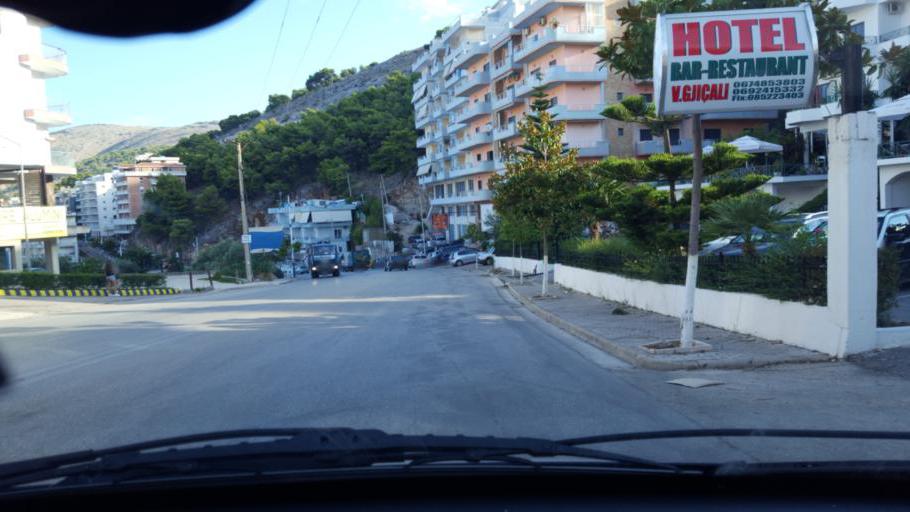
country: AL
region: Vlore
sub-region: Rrethi i Sarandes
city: Sarande
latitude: 39.8695
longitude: 20.0191
